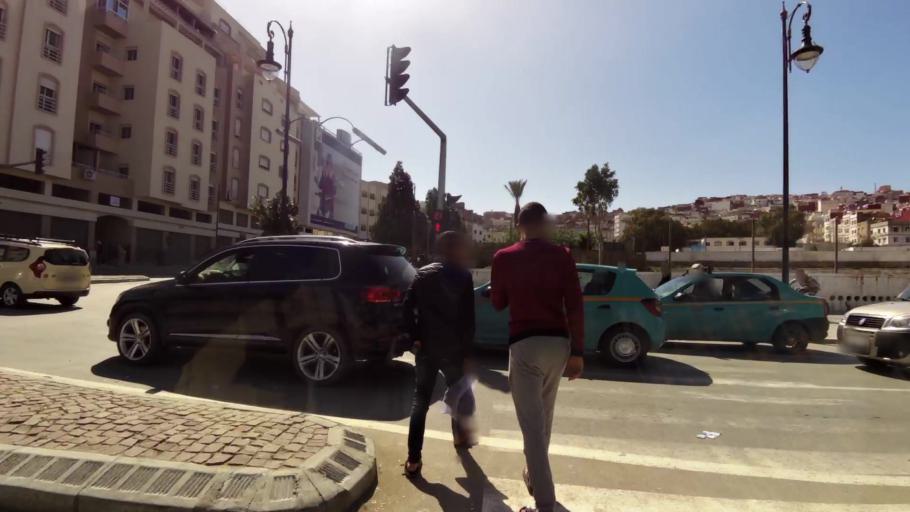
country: MA
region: Tanger-Tetouan
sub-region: Tanger-Assilah
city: Tangier
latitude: 35.7418
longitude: -5.8060
